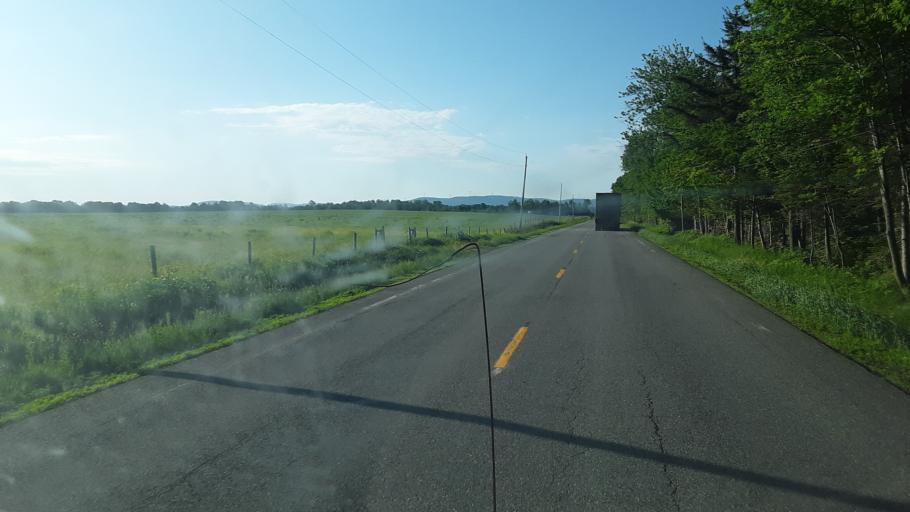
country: US
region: Maine
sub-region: Penobscot County
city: Patten
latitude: 46.1587
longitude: -68.2244
